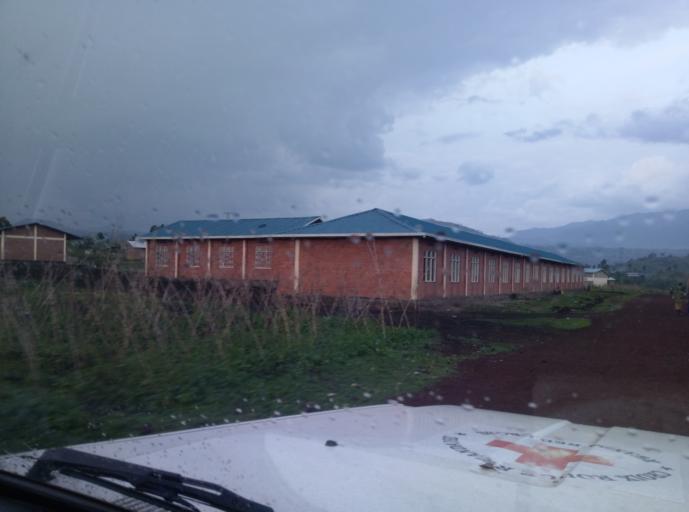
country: RW
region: Western Province
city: Gisenyi
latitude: -1.6549
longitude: 29.2912
